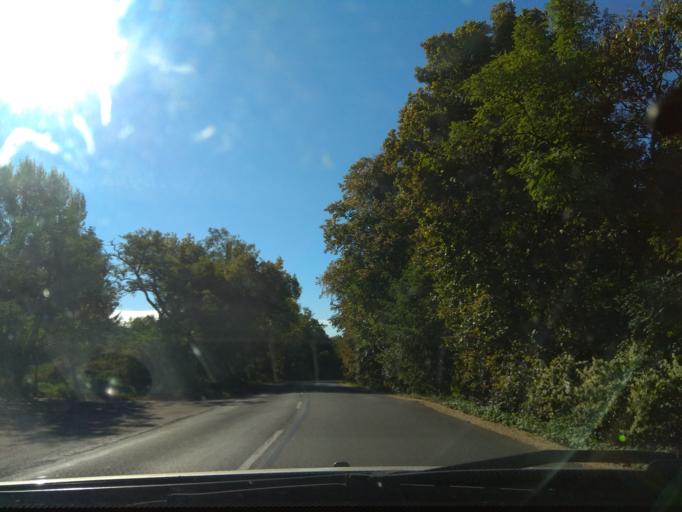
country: HU
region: Borsod-Abauj-Zemplen
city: Miskolc
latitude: 48.0807
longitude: 20.7714
